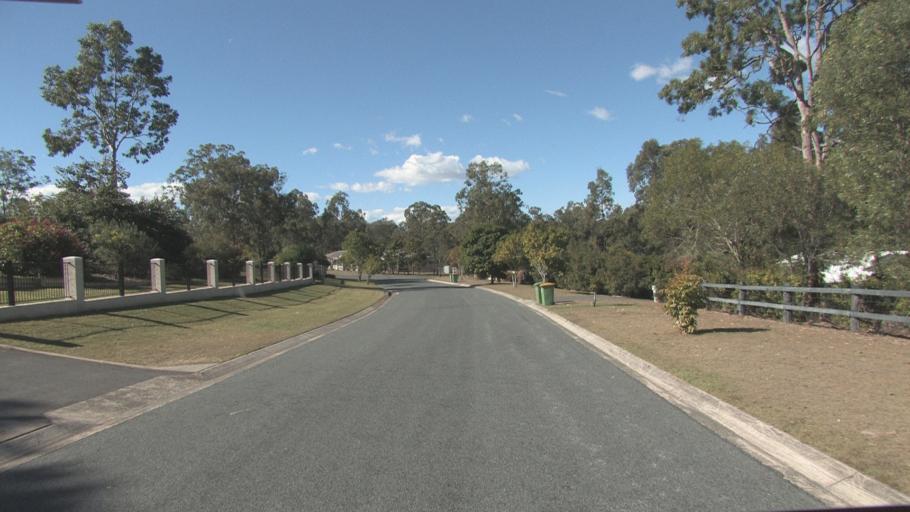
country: AU
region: Queensland
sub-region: Ipswich
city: Springfield Lakes
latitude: -27.7279
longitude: 152.9213
